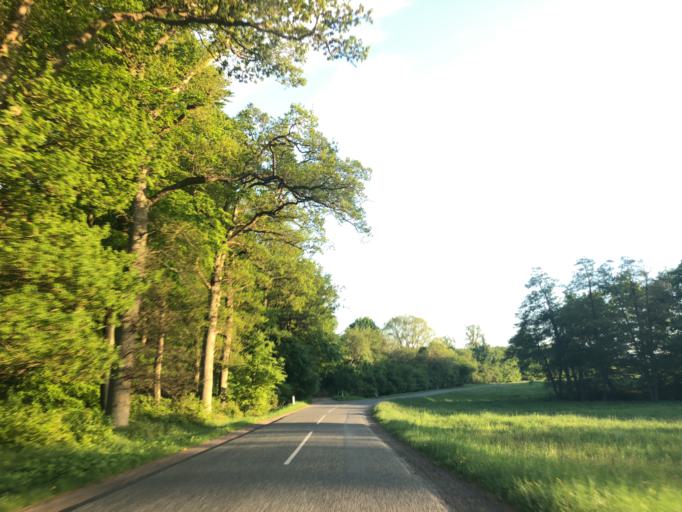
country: DK
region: Zealand
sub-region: Koge Kommune
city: Borup
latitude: 55.4246
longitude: 11.9391
